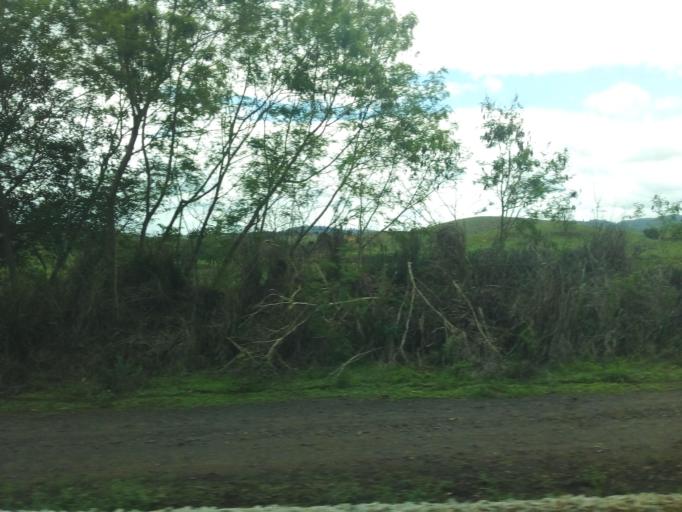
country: BR
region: Minas Gerais
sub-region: Governador Valadares
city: Governador Valadares
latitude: -19.0594
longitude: -42.1477
